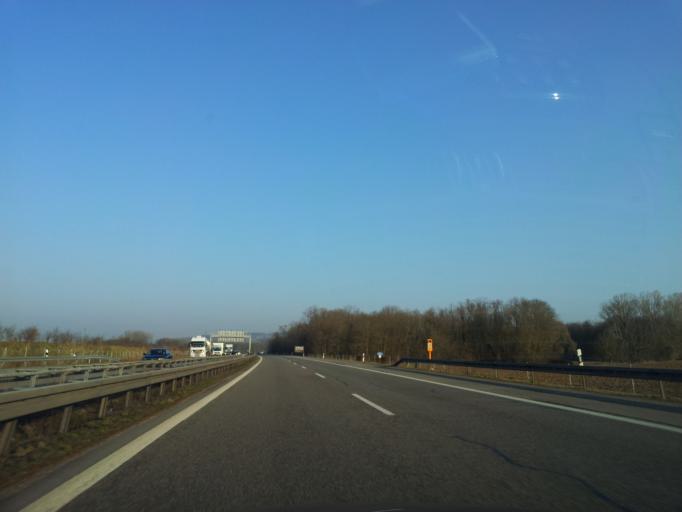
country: DE
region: Baden-Wuerttemberg
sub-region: Freiburg Region
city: Efringen-Kirchen
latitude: 47.6323
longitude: 7.5702
